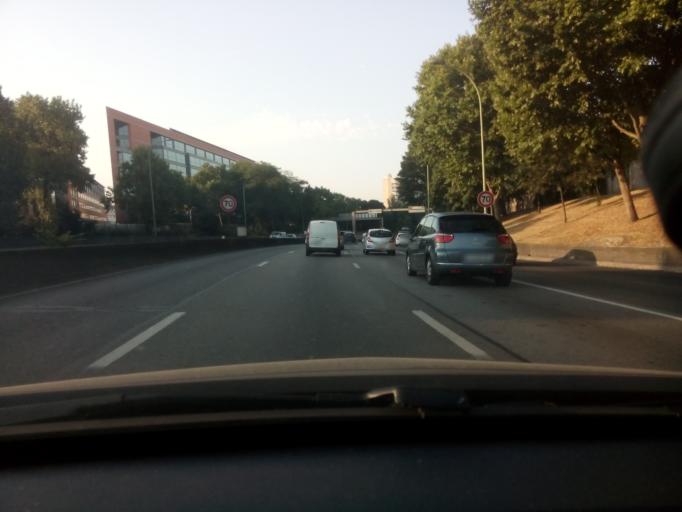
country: FR
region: Ile-de-France
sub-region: Departement du Val-de-Marne
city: Saint-Mande
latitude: 48.8520
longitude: 2.4149
